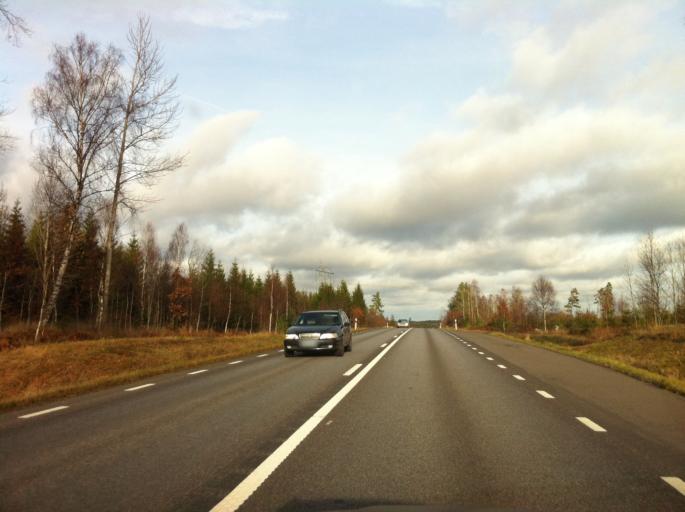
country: SE
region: Kronoberg
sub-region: Vaxjo Kommun
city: Gemla
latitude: 56.7795
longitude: 14.5707
